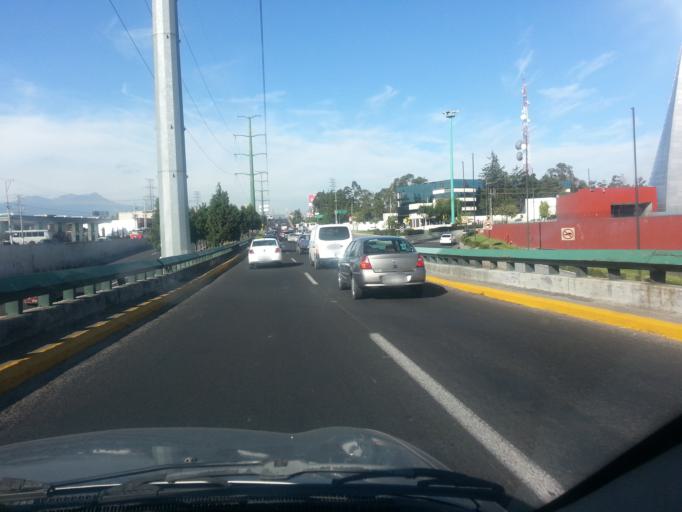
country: MX
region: Mexico
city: Toluca
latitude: 19.2876
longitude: -99.6284
